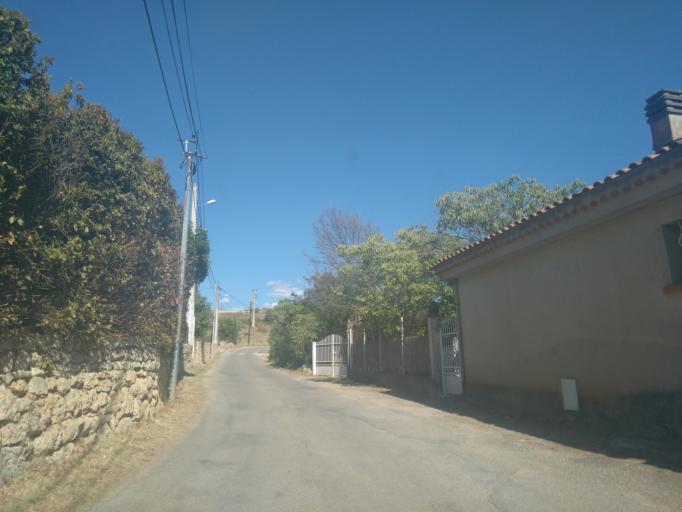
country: FR
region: Provence-Alpes-Cote d'Azur
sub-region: Departement du Var
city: Regusse
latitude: 43.7033
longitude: 6.0926
